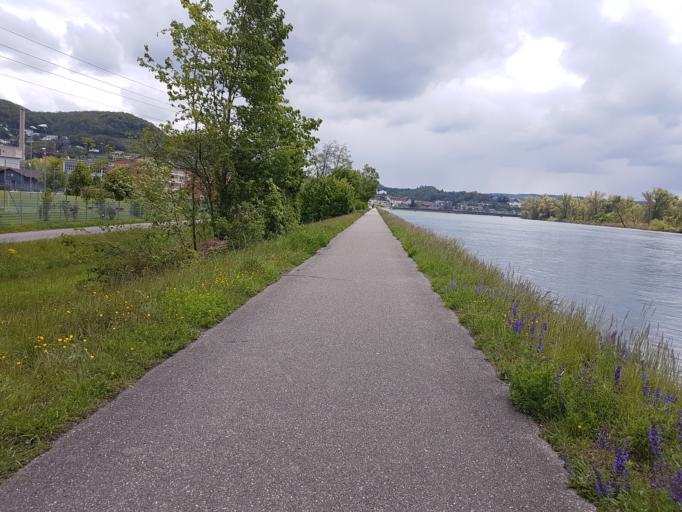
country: CH
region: Aargau
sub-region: Bezirk Zurzach
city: Klingnau
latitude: 47.5784
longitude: 8.2472
